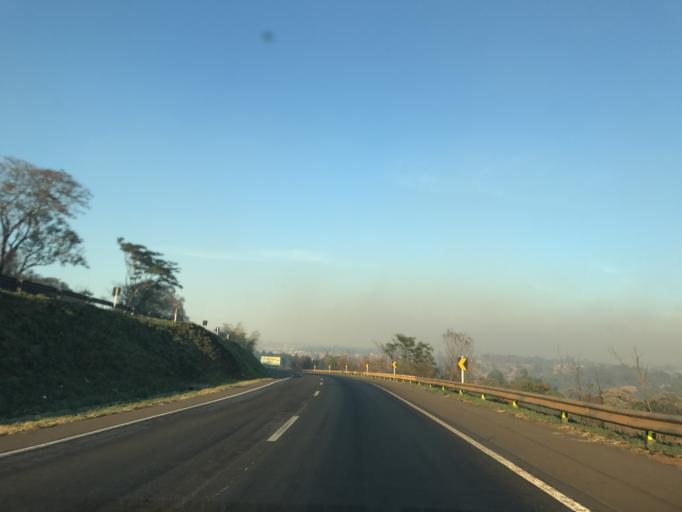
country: BR
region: Goias
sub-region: Goiania
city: Goiania
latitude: -16.5841
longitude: -49.1914
